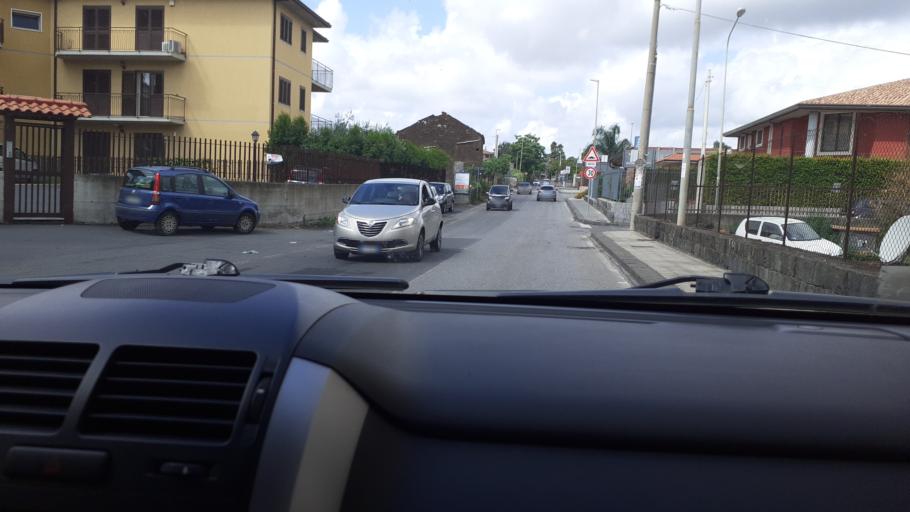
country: IT
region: Sicily
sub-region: Catania
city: San Giovanni la Punta
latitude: 37.5783
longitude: 15.1029
